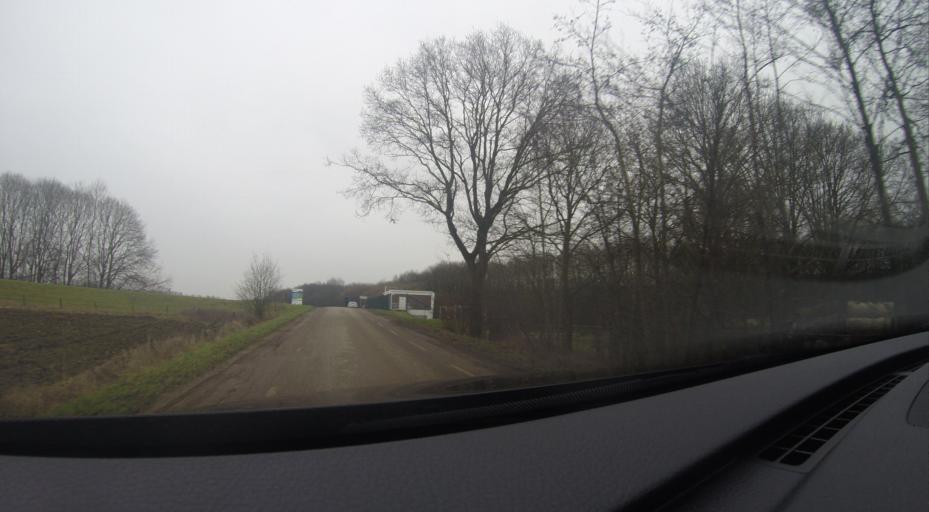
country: NL
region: Gelderland
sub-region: Gemeente Zutphen
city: Zutphen
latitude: 52.1181
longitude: 6.1778
